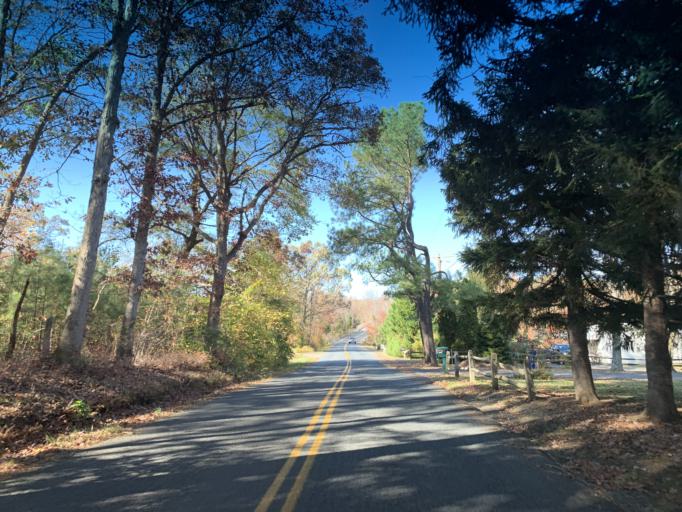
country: US
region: Maryland
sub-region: Harford County
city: Joppatowne
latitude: 39.4426
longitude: -76.3336
